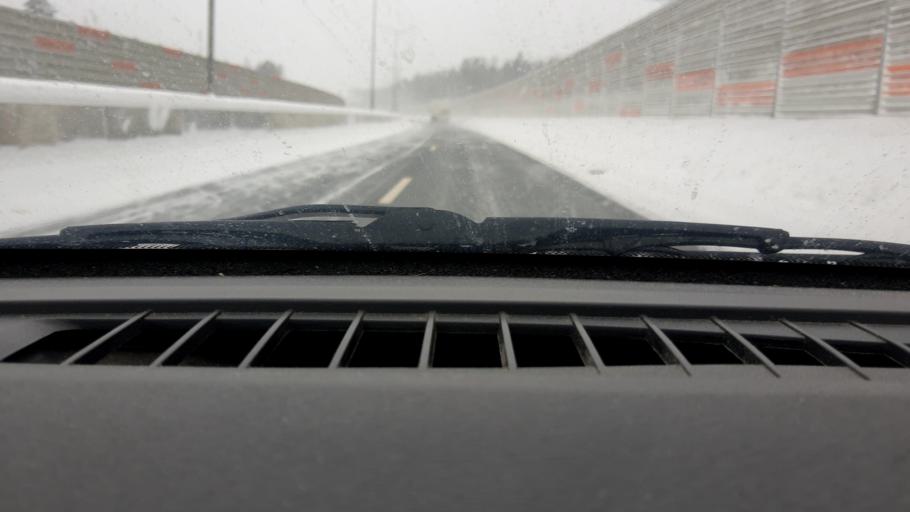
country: RU
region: Moskovskaya
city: Krasnoarmeysk
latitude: 56.0402
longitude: 38.1956
